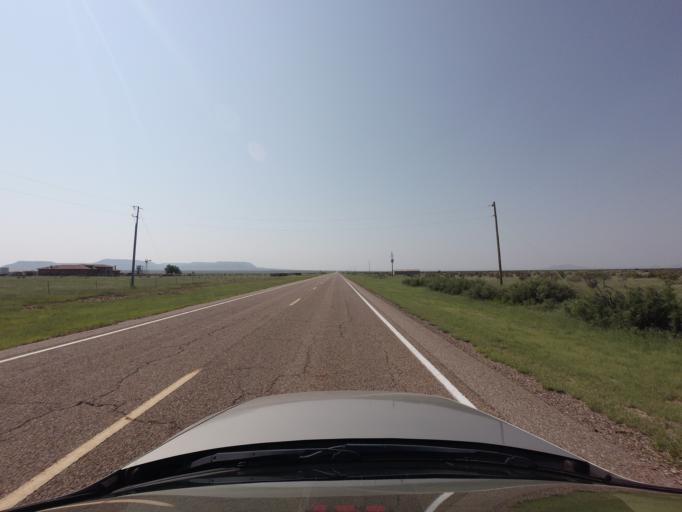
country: US
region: New Mexico
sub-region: Quay County
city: Tucumcari
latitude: 35.0521
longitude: -103.7375
